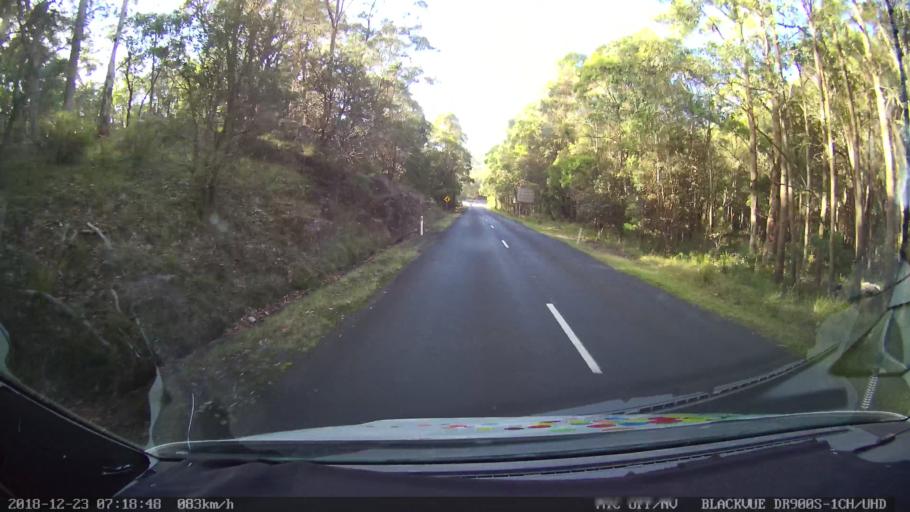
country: AU
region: New South Wales
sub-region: Bellingen
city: Dorrigo
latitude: -30.4788
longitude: 152.2915
